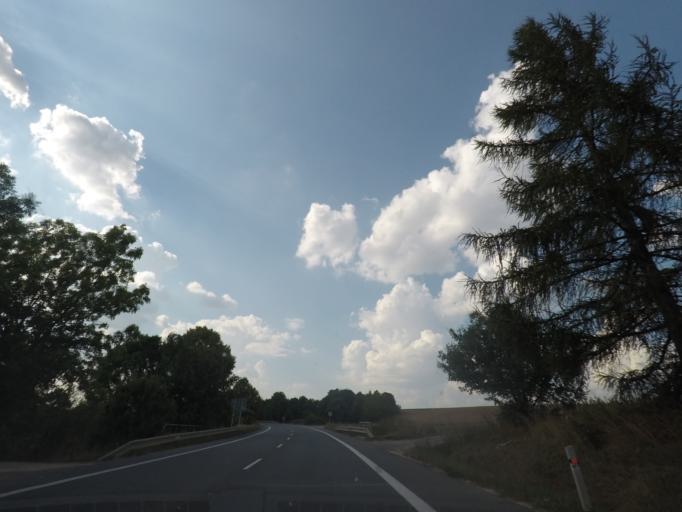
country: CZ
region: Kralovehradecky
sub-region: Okres Nachod
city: Jaromer
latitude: 50.3998
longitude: 15.8965
